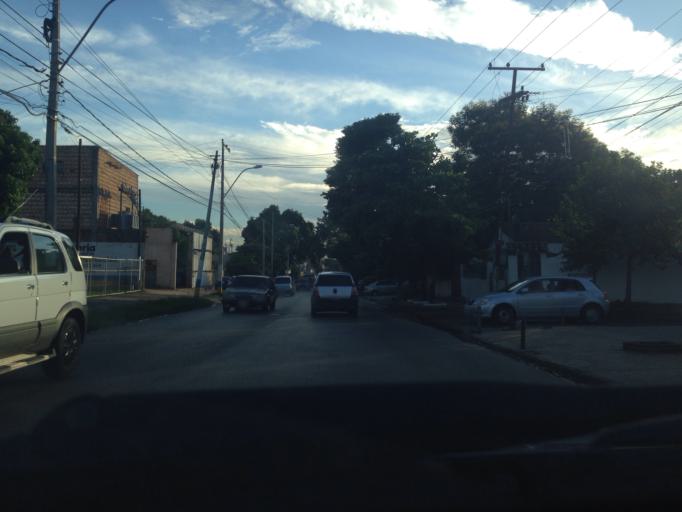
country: PY
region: Central
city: Lambare
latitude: -25.3318
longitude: -57.5878
